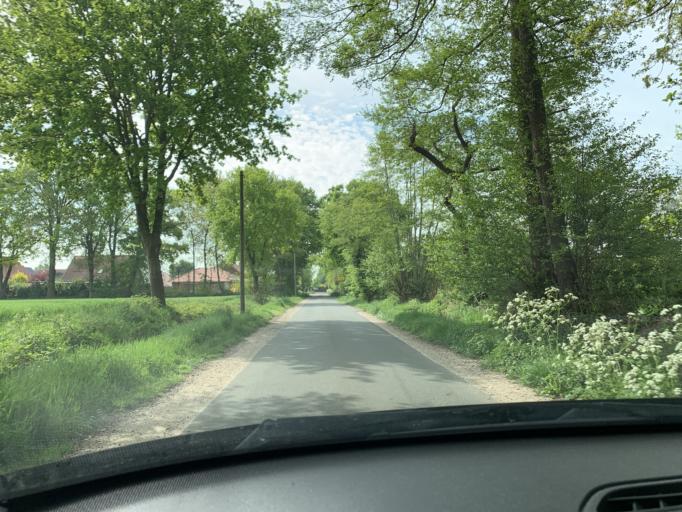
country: DE
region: Lower Saxony
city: Apen
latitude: 53.2280
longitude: 7.8134
